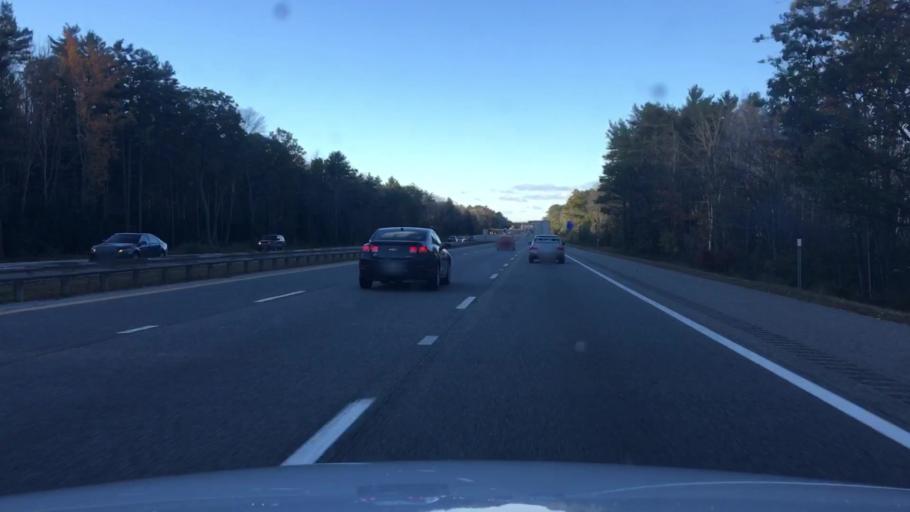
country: US
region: Maine
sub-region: York County
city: West Kennebunk
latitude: 43.4517
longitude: -70.5316
